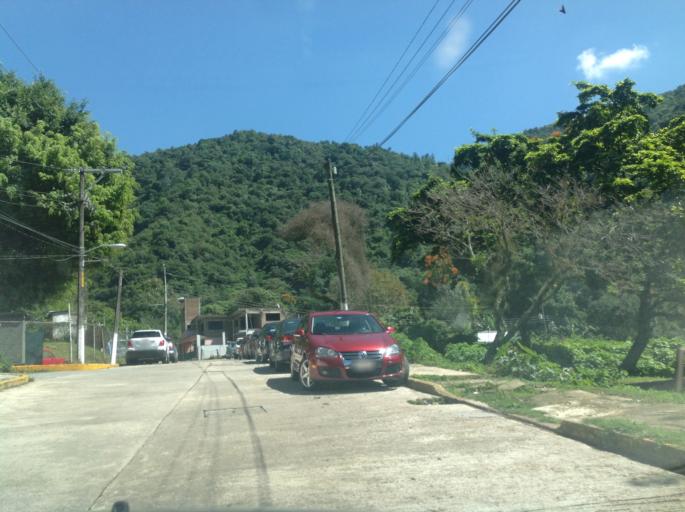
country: MX
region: Veracruz
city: Nogales
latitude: 18.8451
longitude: -97.1605
